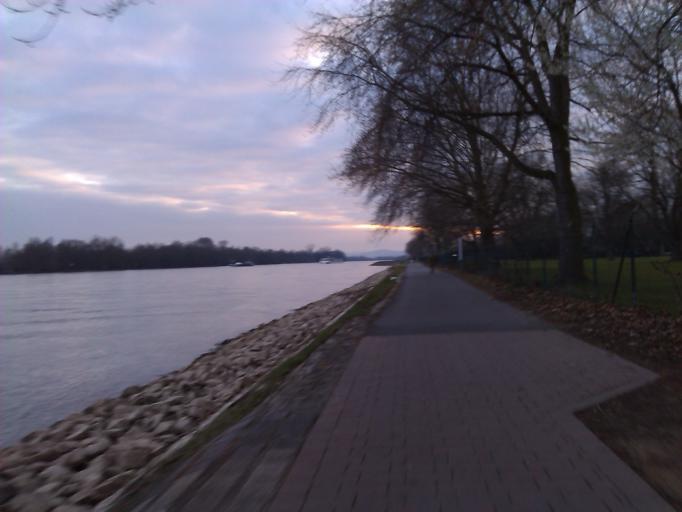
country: DE
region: Hesse
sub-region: Regierungsbezirk Darmstadt
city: Eltville
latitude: 50.0211
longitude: 8.1091
